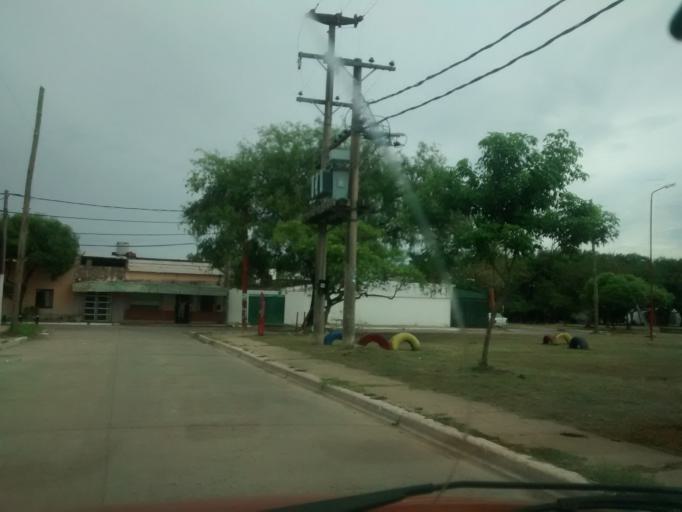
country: AR
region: Chaco
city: Resistencia
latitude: -27.4562
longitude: -59.0169
